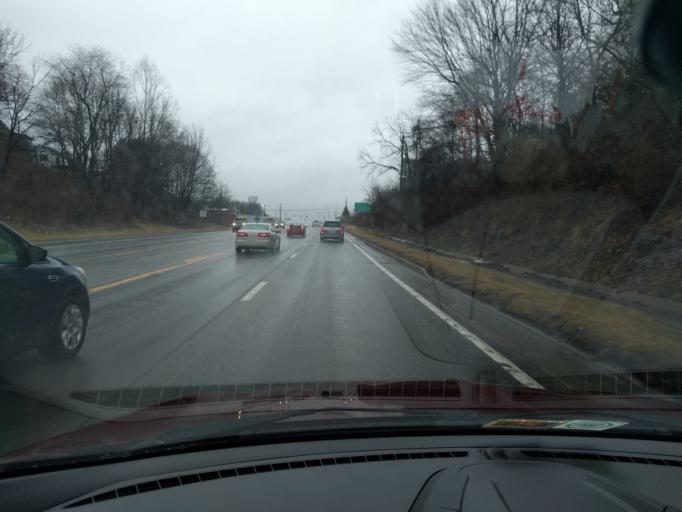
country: US
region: West Virginia
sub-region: Raleigh County
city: Beckley
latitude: 37.7909
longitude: -81.1844
